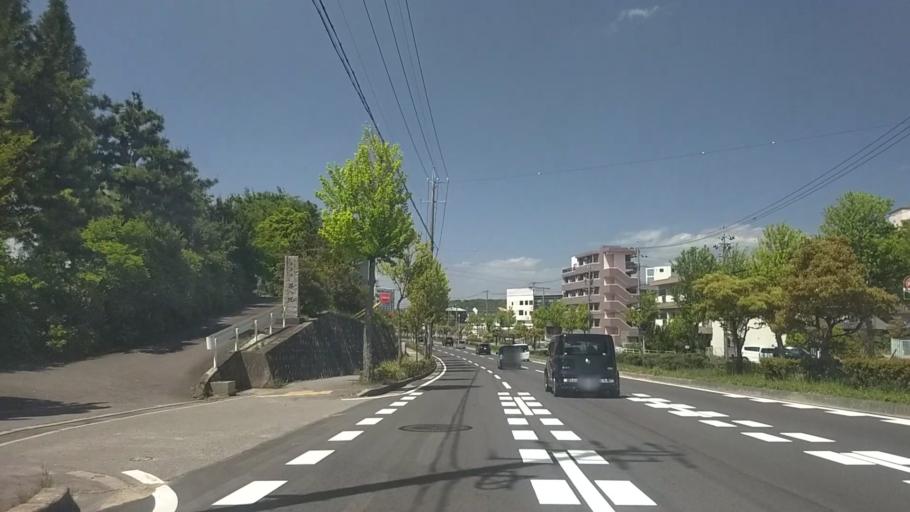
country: JP
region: Aichi
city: Okazaki
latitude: 34.9561
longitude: 137.1897
